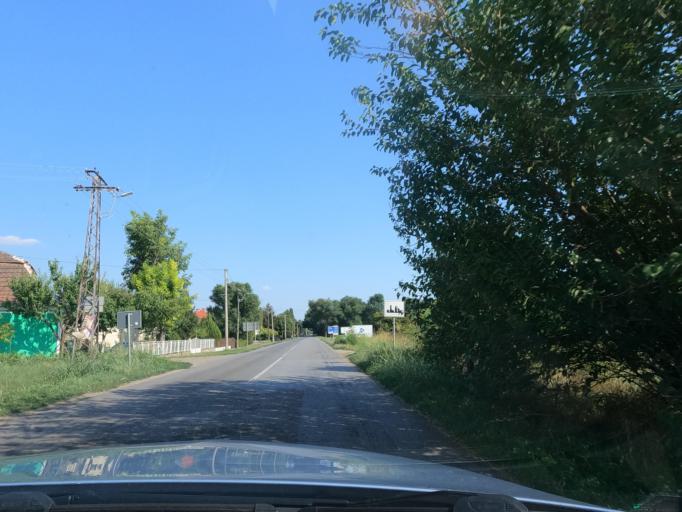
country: RS
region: Autonomna Pokrajina Vojvodina
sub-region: Juznobacki Okrug
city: Becej
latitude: 45.6311
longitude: 20.0165
